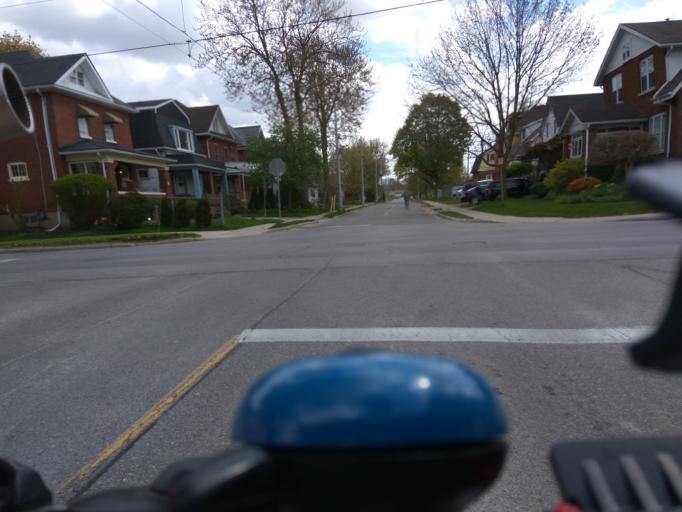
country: CA
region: Ontario
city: Stratford
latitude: 43.3674
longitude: -80.9736
